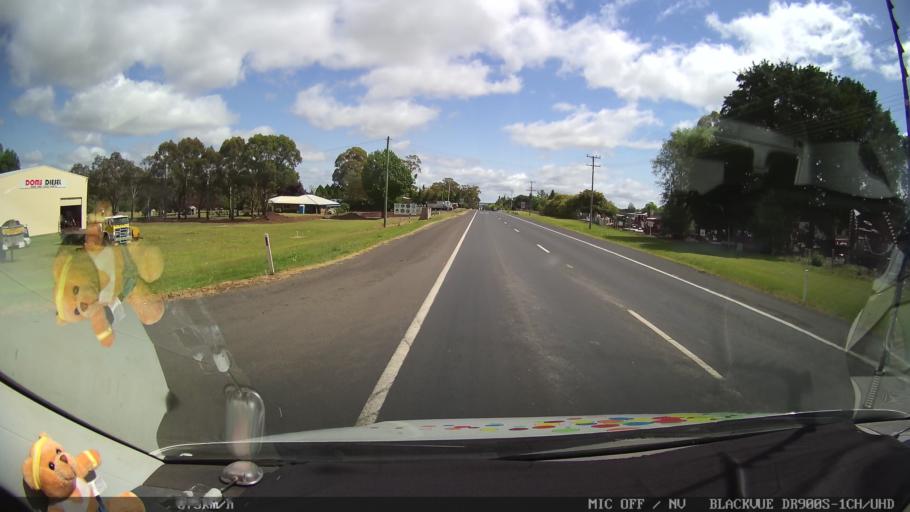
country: AU
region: New South Wales
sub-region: Glen Innes Severn
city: Glen Innes
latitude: -29.7654
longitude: 151.7331
